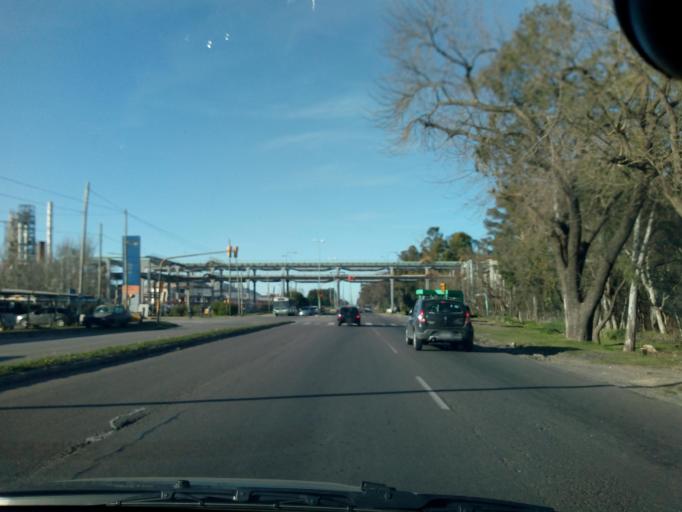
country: AR
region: Buenos Aires
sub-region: Partido de Ensenada
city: Ensenada
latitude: -34.8805
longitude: -57.9233
